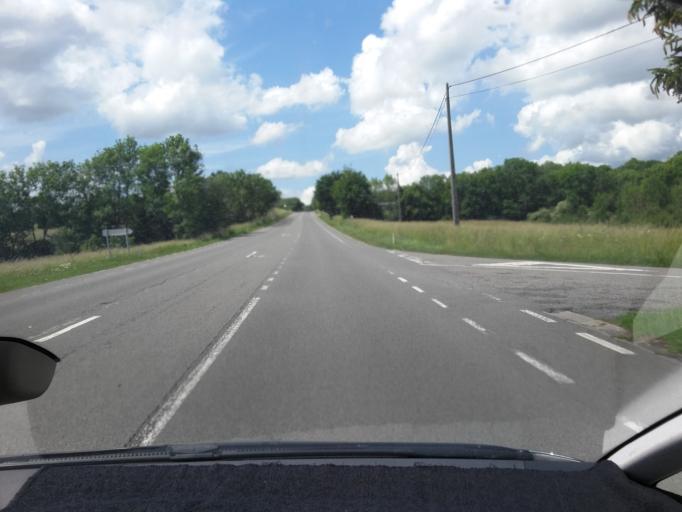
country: BE
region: Wallonia
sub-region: Province de Namur
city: Rochefort
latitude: 50.2179
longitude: 5.1875
